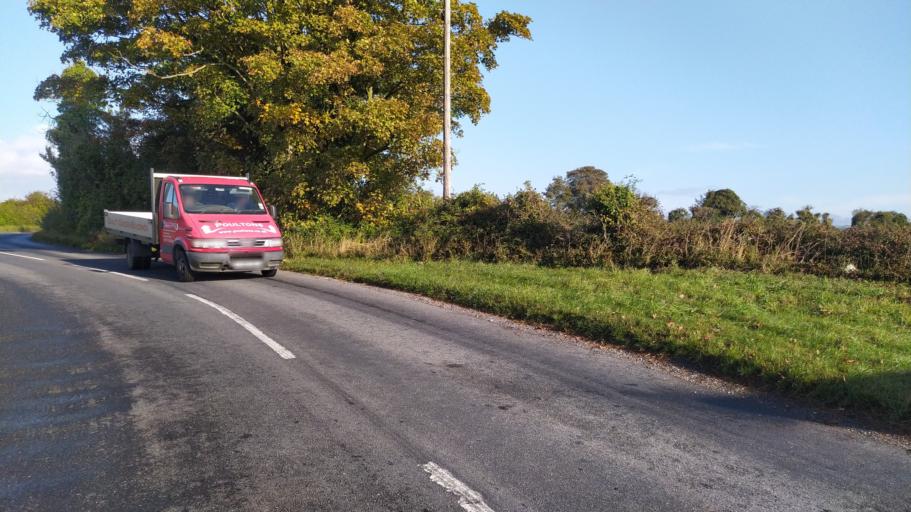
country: GB
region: England
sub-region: Wiltshire
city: Bower Chalke
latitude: 50.9170
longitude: -2.0503
